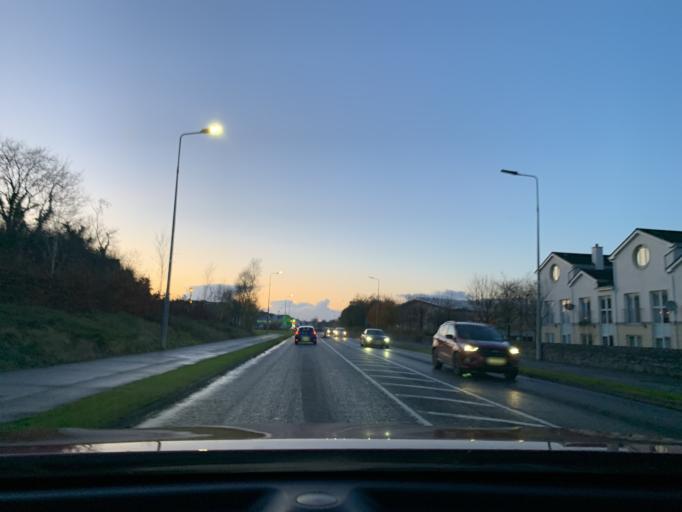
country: IE
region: Connaught
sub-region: County Leitrim
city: Carrick-on-Shannon
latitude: 53.9415
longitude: -8.1012
